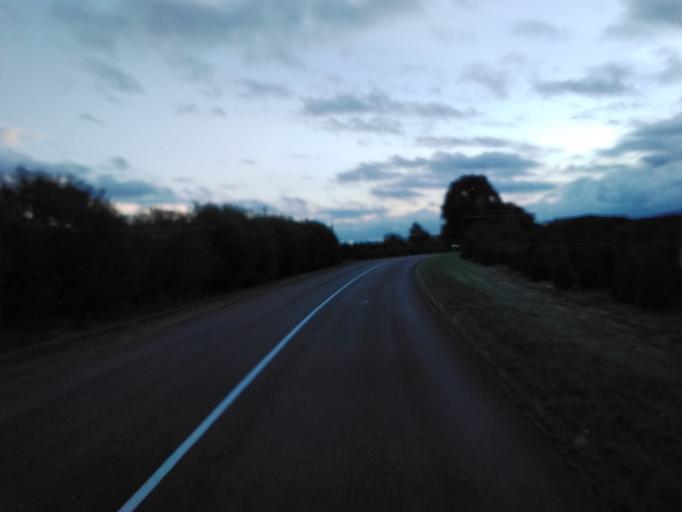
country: FR
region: Bourgogne
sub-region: Departement de la Cote-d'Or
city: Saulieu
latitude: 47.2616
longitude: 4.2070
